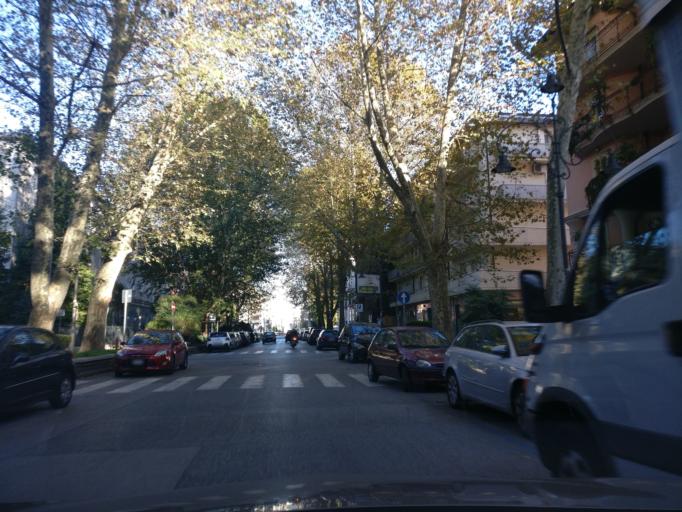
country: IT
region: Campania
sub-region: Provincia di Avellino
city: Avellino
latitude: 40.9131
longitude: 14.7819
